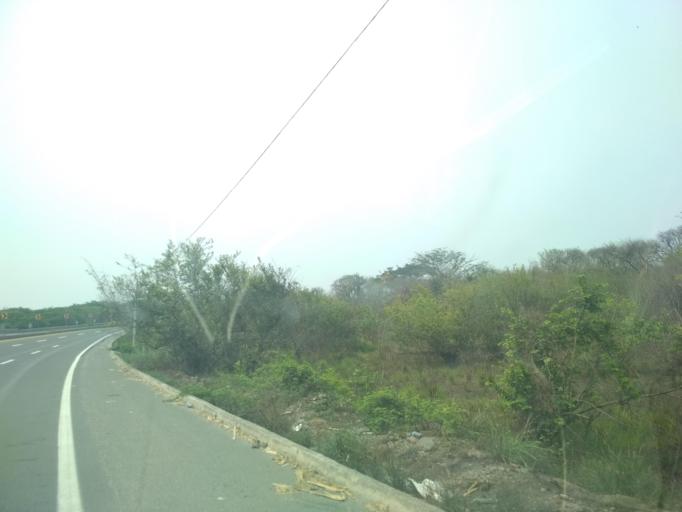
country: MX
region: Veracruz
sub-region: Veracruz
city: Delfino Victoria (Santa Fe)
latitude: 19.1941
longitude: -96.2752
